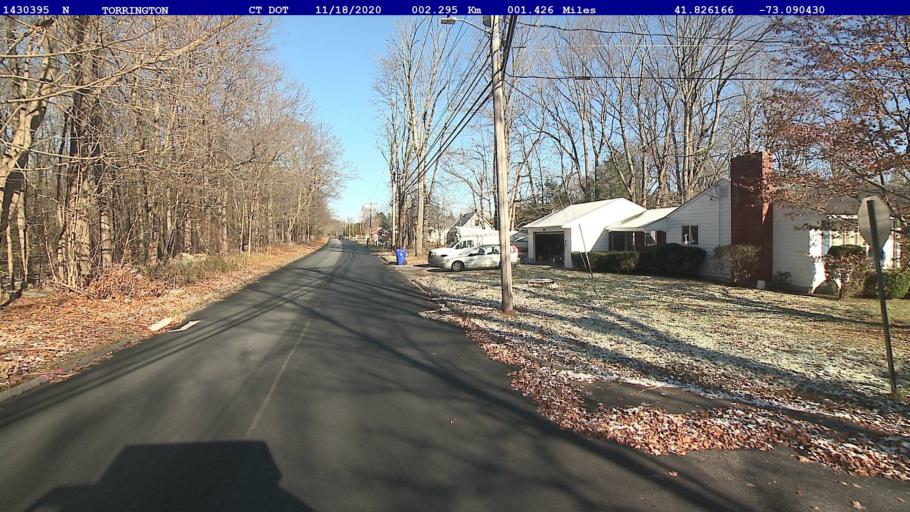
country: US
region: Connecticut
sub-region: Litchfield County
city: Torrington
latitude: 41.8262
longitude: -73.0904
